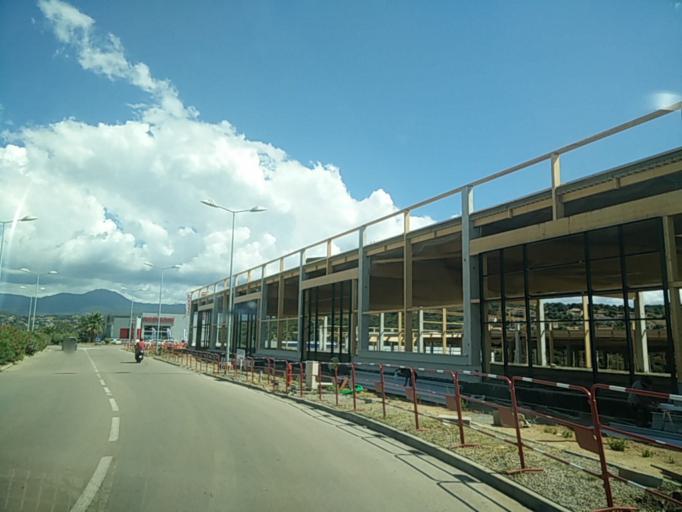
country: FR
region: Corsica
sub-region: Departement de la Corse-du-Sud
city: Afa
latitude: 41.9537
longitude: 8.7973
